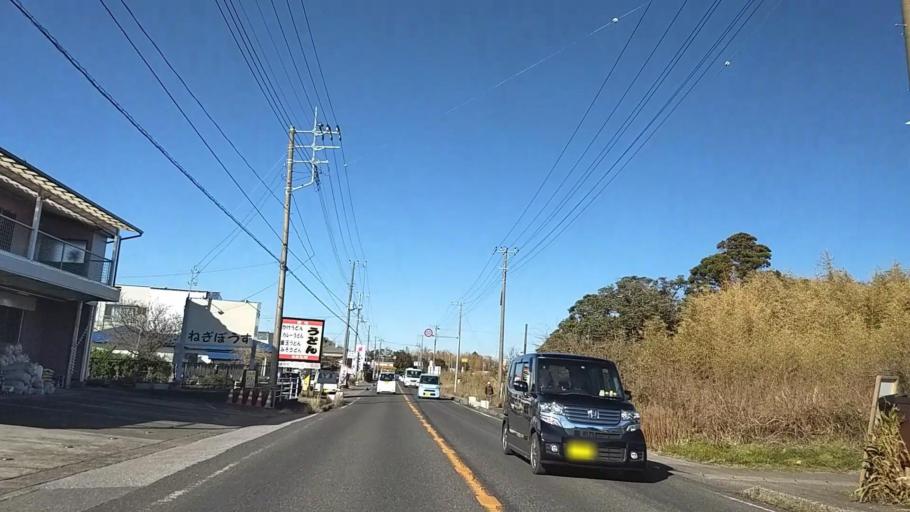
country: JP
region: Chiba
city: Ohara
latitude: 35.2848
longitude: 140.3924
